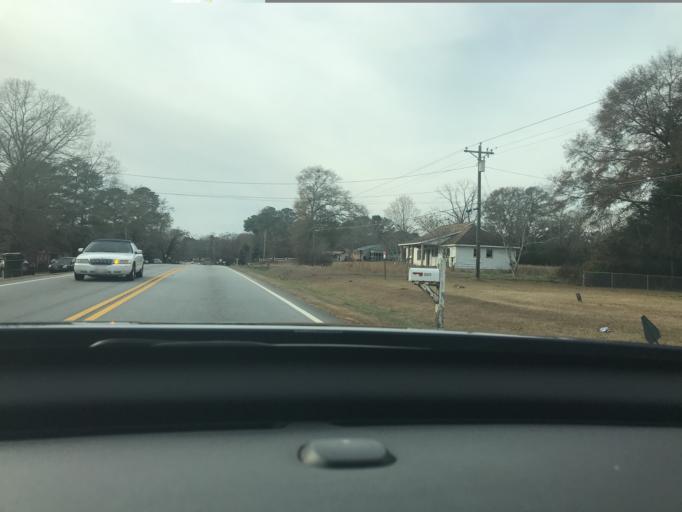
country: US
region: Georgia
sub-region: Newton County
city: Porterdale
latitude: 33.5796
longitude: -83.9325
